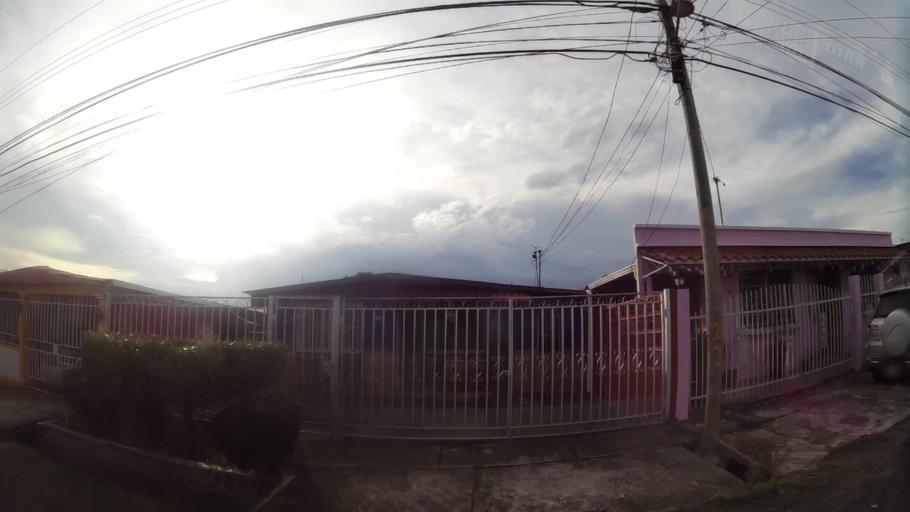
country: PA
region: Panama
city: La Chorrera
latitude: 8.8963
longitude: -79.7653
